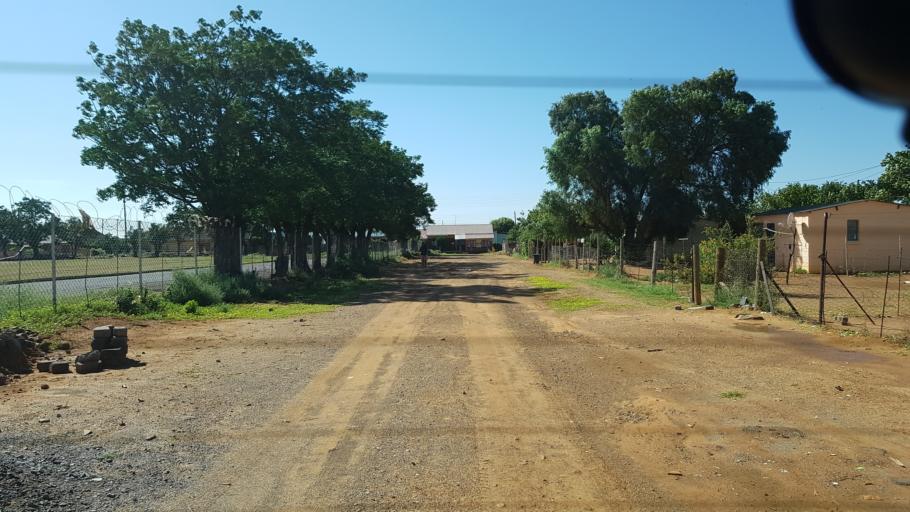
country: ZA
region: Northern Cape
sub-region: Siyanda District Municipality
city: Danielskuil
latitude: -28.1917
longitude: 23.5372
